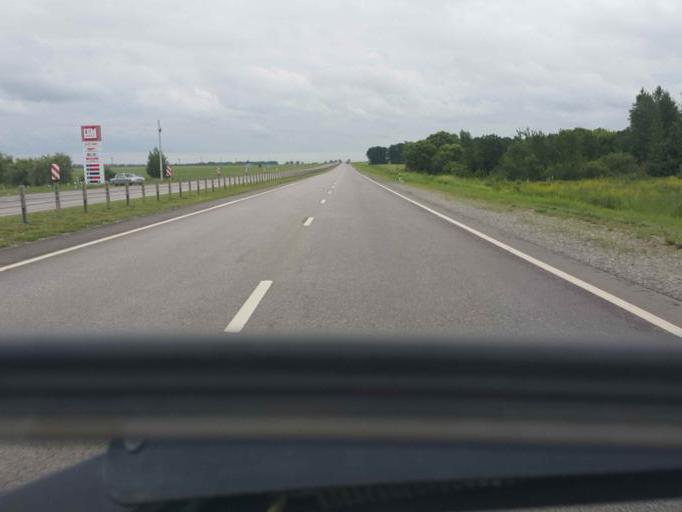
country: RU
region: Tambov
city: Zavoronezhskoye
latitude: 52.9006
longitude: 40.6622
